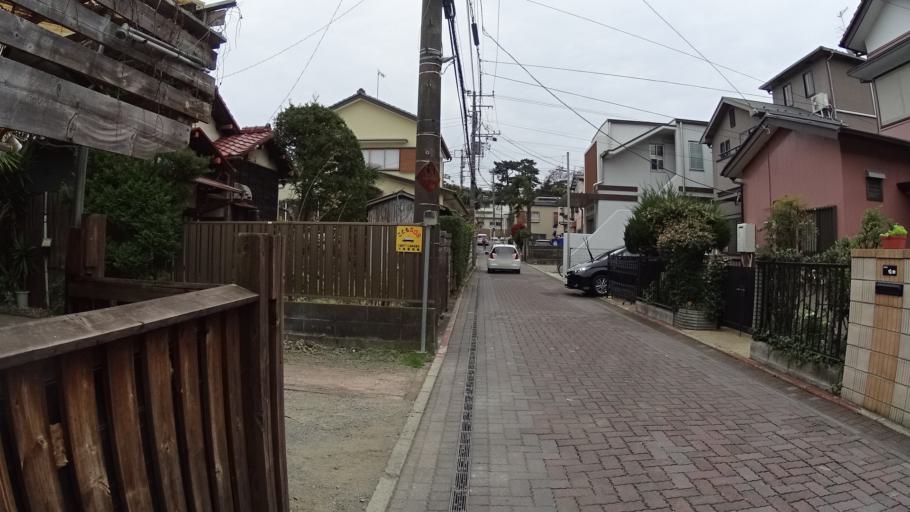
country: JP
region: Kanagawa
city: Oiso
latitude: 35.3088
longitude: 139.3082
